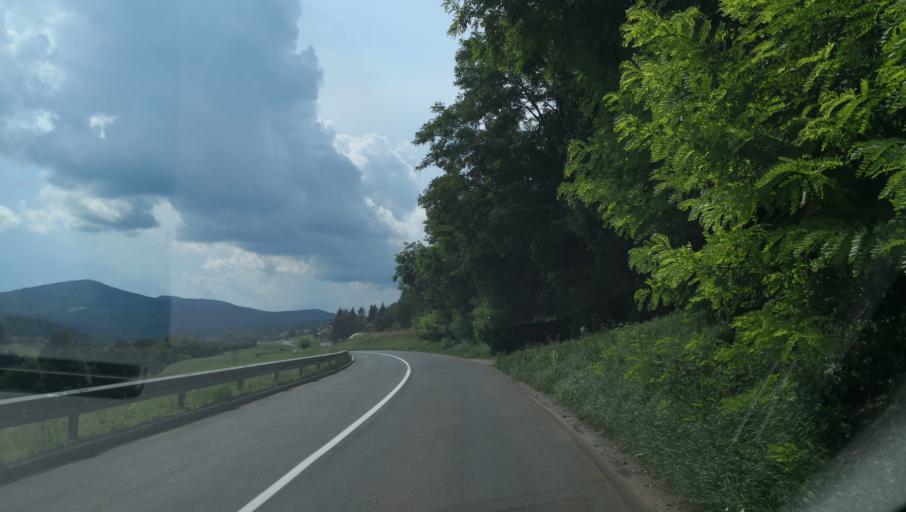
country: SI
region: Zuzemberk
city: Zuzemberk
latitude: 45.8566
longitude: 14.8753
